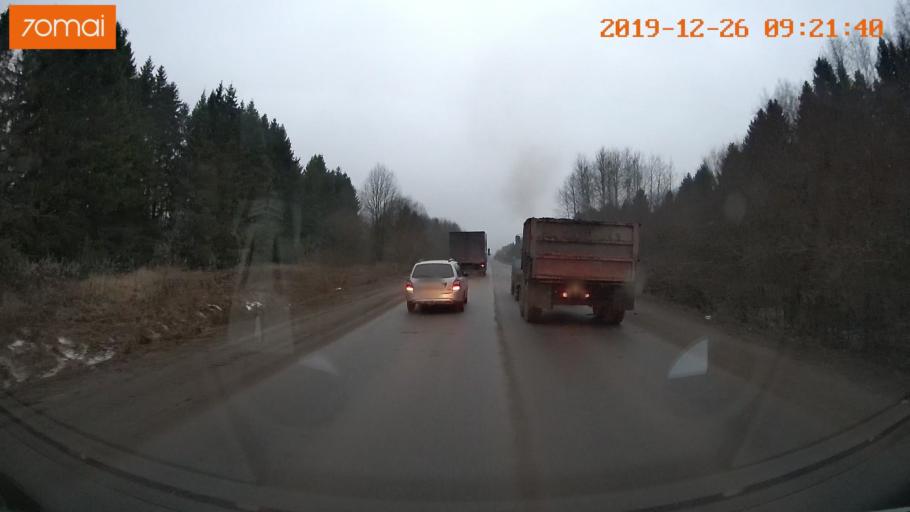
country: RU
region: Vologda
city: Gryazovets
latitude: 58.9715
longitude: 40.2233
